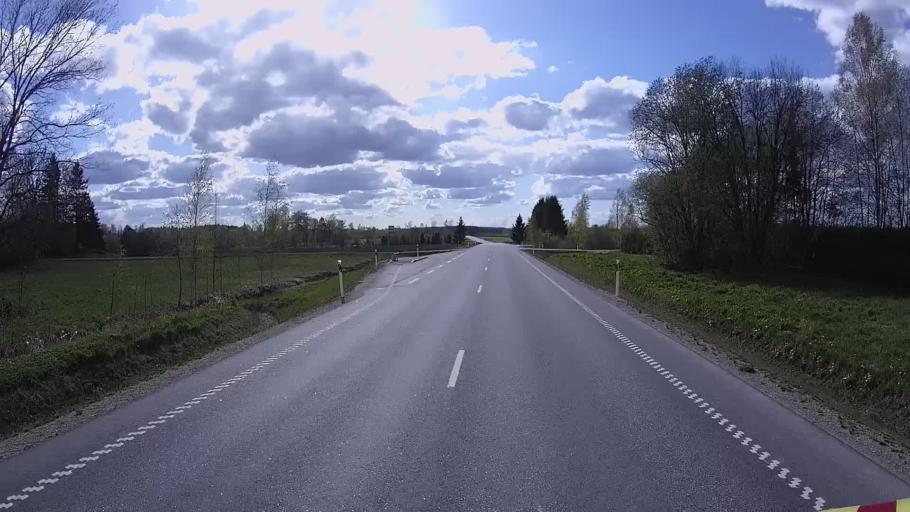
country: EE
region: Jogevamaa
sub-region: Mustvee linn
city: Mustvee
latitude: 58.8312
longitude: 26.7822
